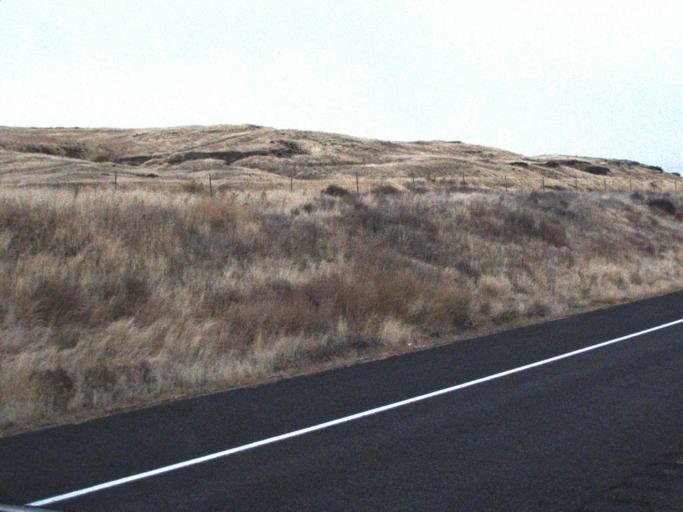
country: US
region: Washington
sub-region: Adams County
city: Ritzville
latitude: 46.7429
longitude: -118.2175
